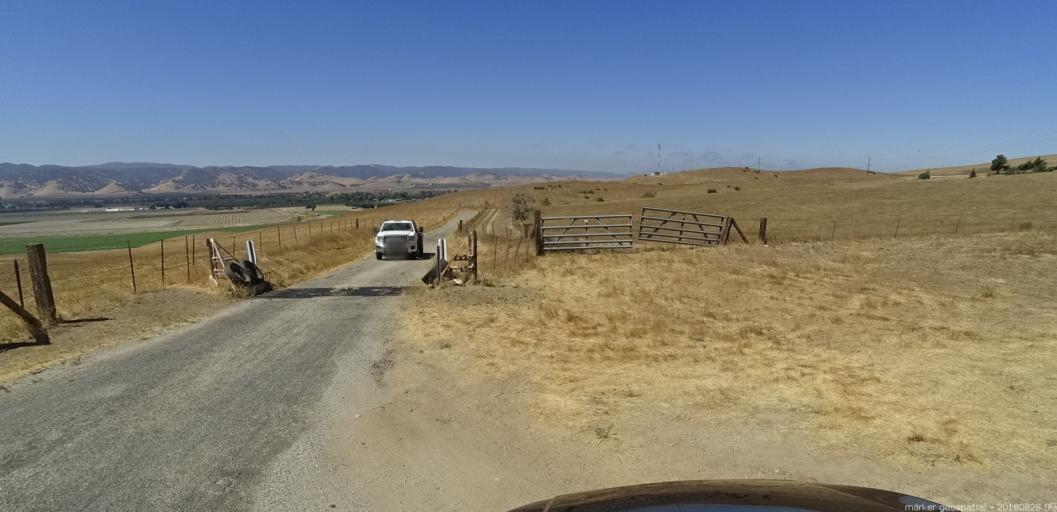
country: US
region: California
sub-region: San Luis Obispo County
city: Lake Nacimiento
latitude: 36.0231
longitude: -120.8861
